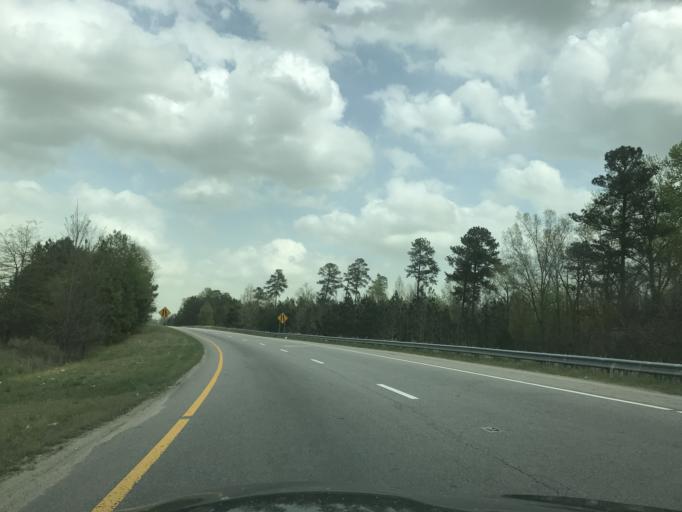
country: US
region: North Carolina
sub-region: Wake County
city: Raleigh
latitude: 35.8734
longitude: -78.5768
